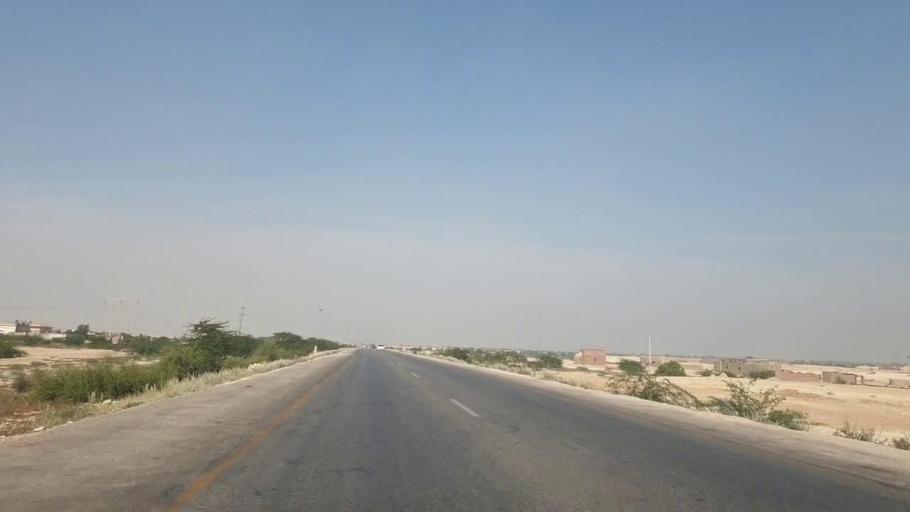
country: PK
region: Sindh
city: Hala
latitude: 25.8036
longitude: 68.2777
